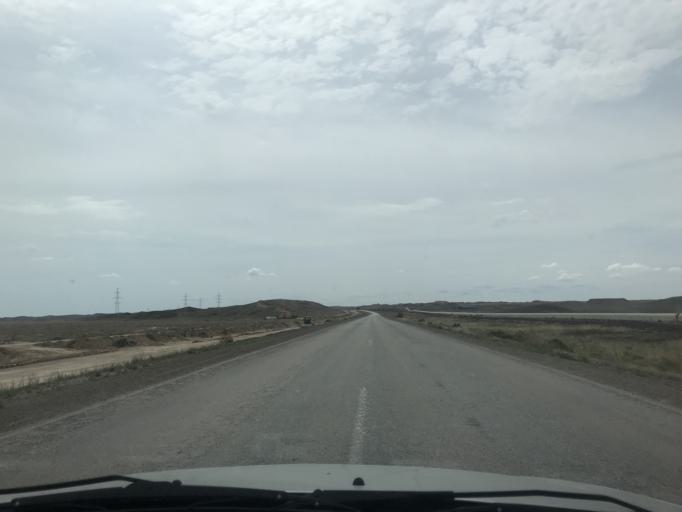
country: KZ
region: Zhambyl
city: Mynaral
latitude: 45.3781
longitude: 73.6540
